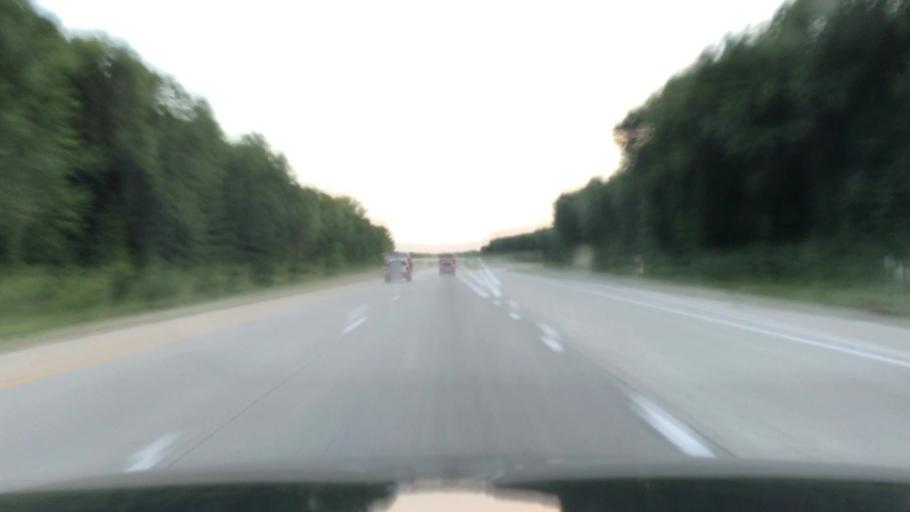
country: US
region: Michigan
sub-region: Montcalm County
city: Howard City
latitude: 43.4017
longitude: -85.5124
